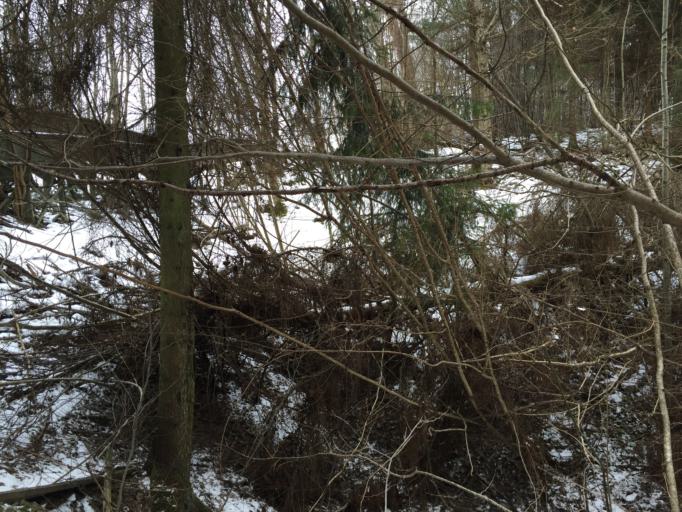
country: LV
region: Seja
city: Loja
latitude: 57.1437
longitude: 24.6819
